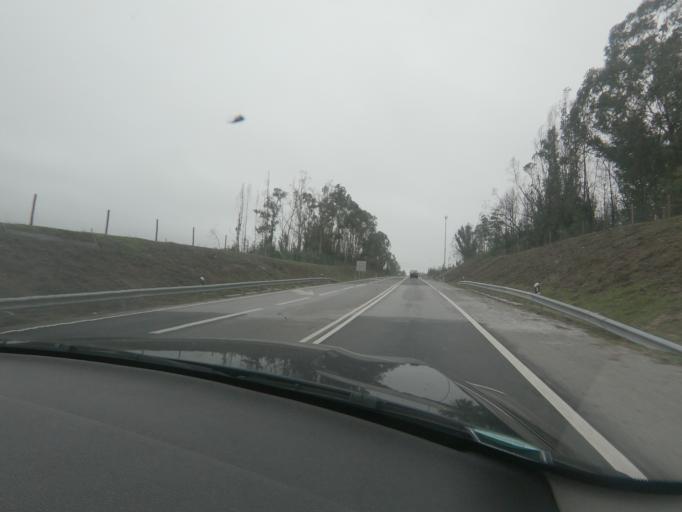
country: PT
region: Viseu
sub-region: Concelho de Tondela
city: Tondela
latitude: 40.5632
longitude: -8.0507
